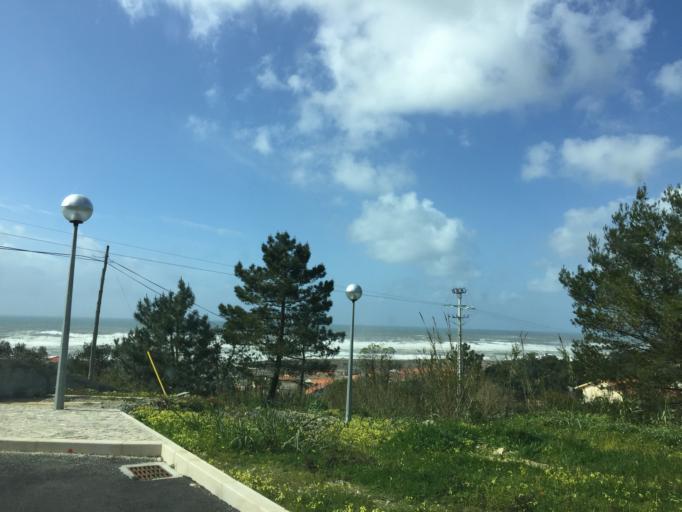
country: PT
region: Coimbra
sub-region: Figueira da Foz
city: Buarcos
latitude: 40.2075
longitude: -8.8927
